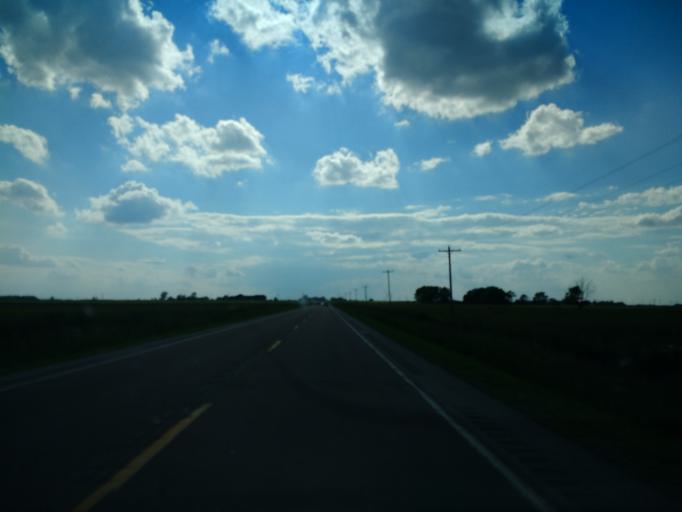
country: US
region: Iowa
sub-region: Clay County
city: Spencer
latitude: 43.1837
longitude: -95.2234
